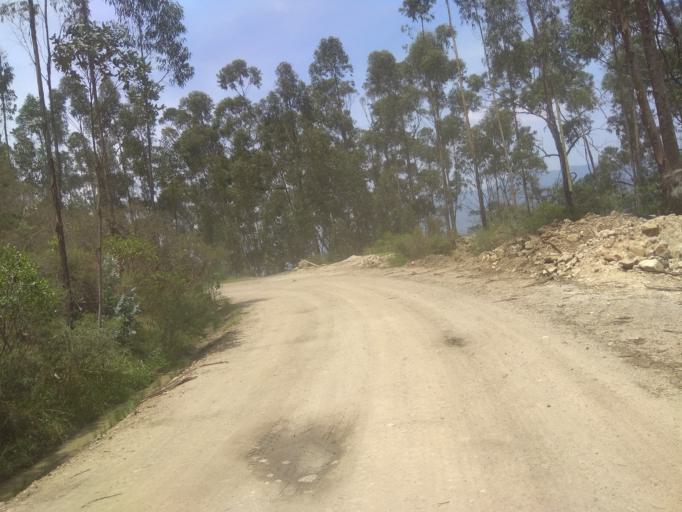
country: CO
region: Boyaca
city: Socha Viejo
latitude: 5.9797
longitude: -72.7355
